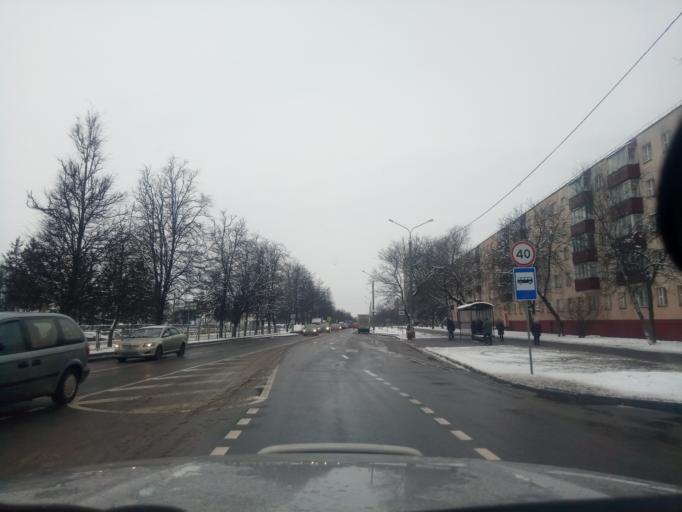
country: BY
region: Minsk
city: Hatava
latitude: 53.8344
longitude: 27.6279
